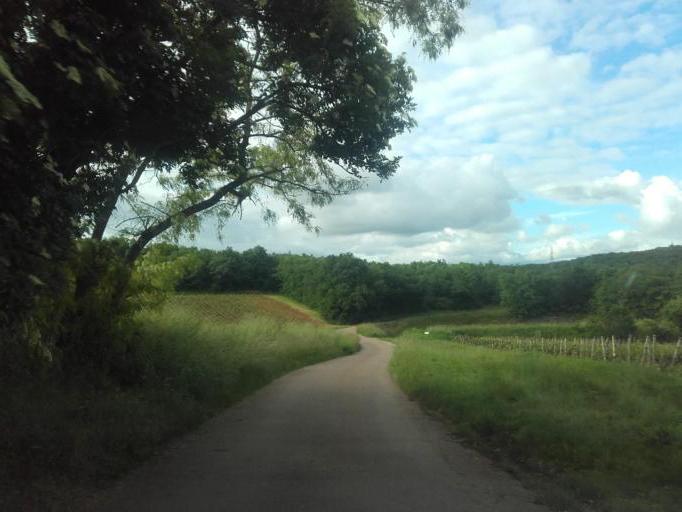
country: FR
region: Bourgogne
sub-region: Departement de Saone-et-Loire
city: Rully
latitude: 46.8436
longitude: 4.7365
